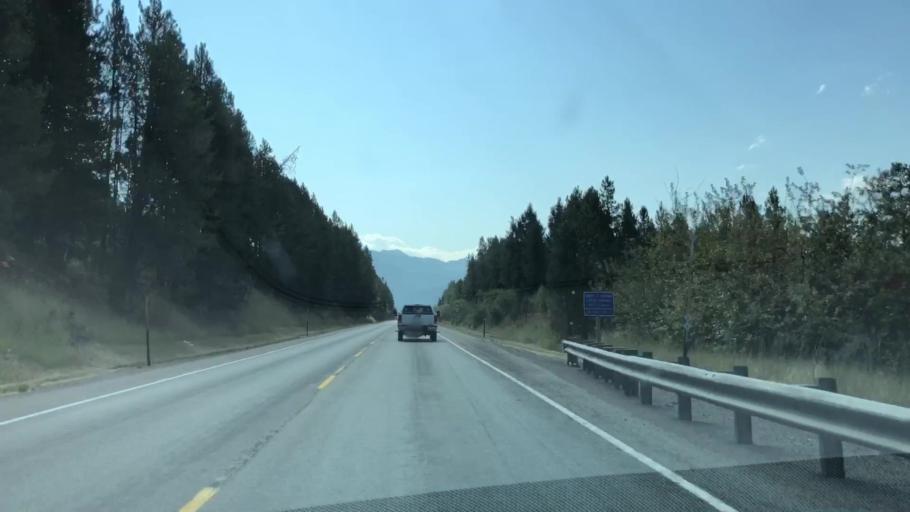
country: US
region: Wyoming
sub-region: Teton County
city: Hoback
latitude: 43.2004
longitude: -111.0438
